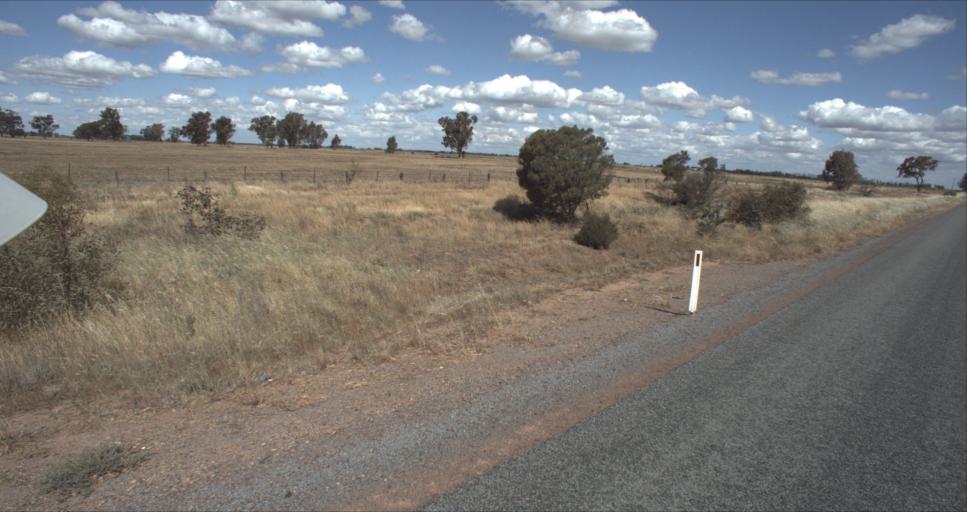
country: AU
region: New South Wales
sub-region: Leeton
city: Leeton
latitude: -34.4908
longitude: 146.2473
